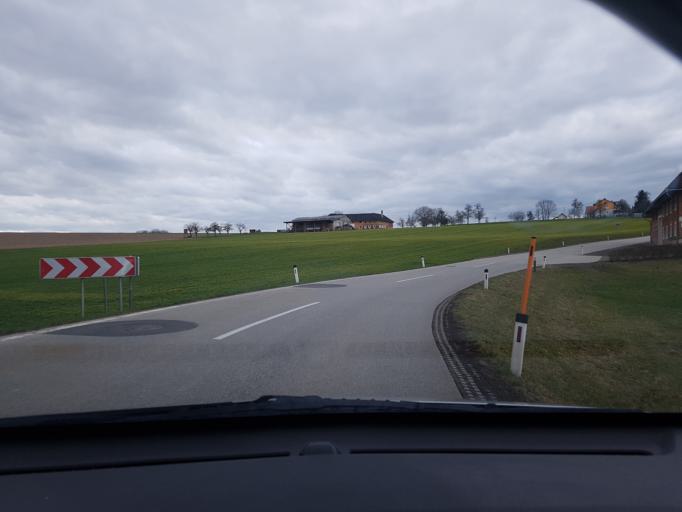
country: AT
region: Upper Austria
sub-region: Politischer Bezirk Linz-Land
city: Ansfelden
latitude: 48.1624
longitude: 14.3129
